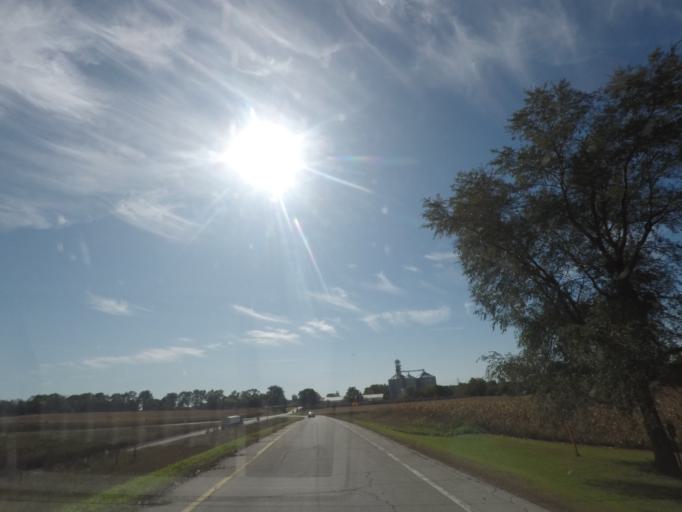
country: US
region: Iowa
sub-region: Story County
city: Nevada
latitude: 42.0220
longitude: -93.3098
